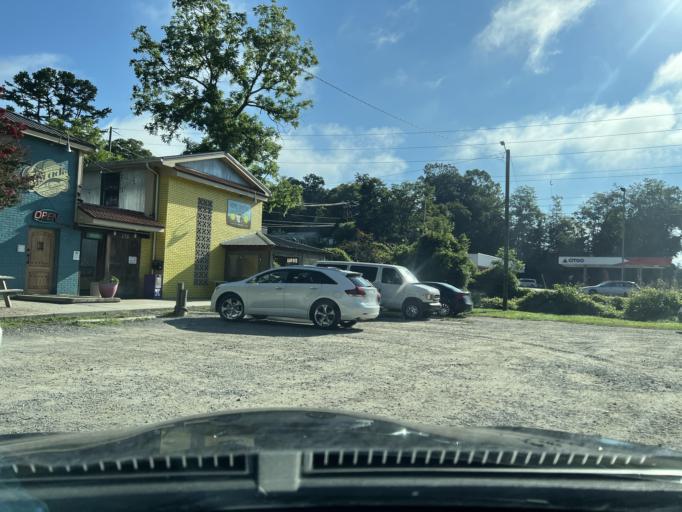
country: US
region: North Carolina
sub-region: Buncombe County
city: Asheville
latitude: 35.5668
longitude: -82.5743
